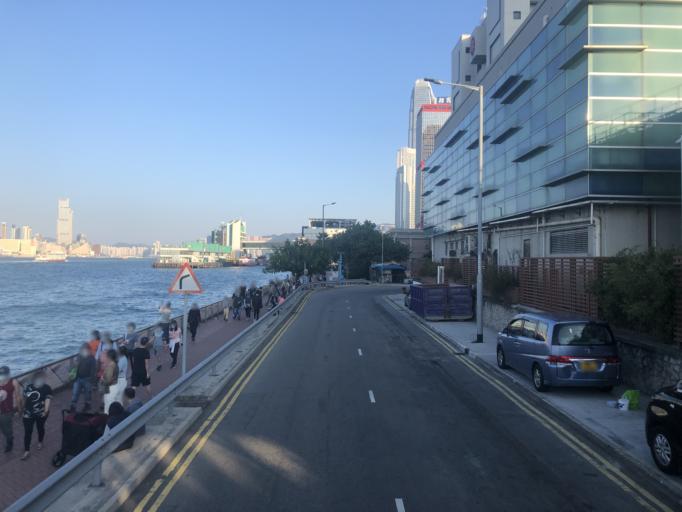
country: HK
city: Hong Kong
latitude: 22.2899
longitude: 114.1479
